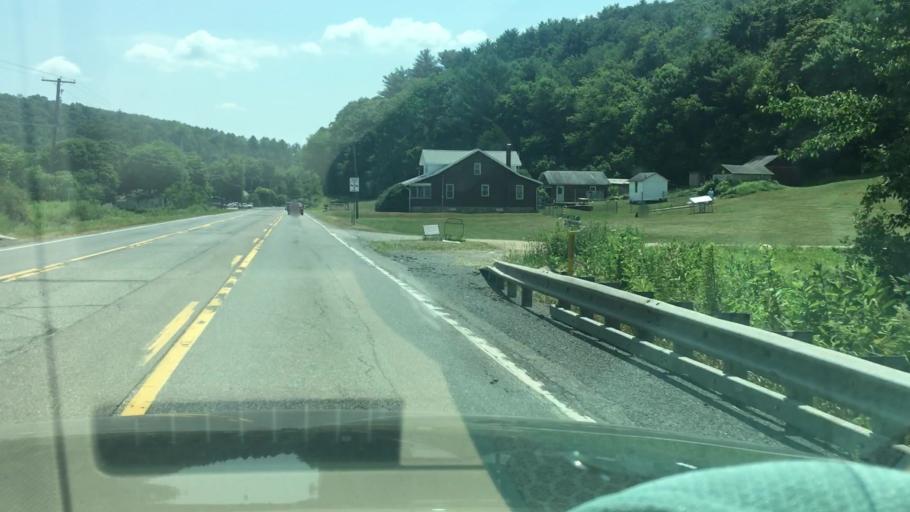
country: US
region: Pennsylvania
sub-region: Schuylkill County
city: Coaldale
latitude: 40.7409
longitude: -75.8885
